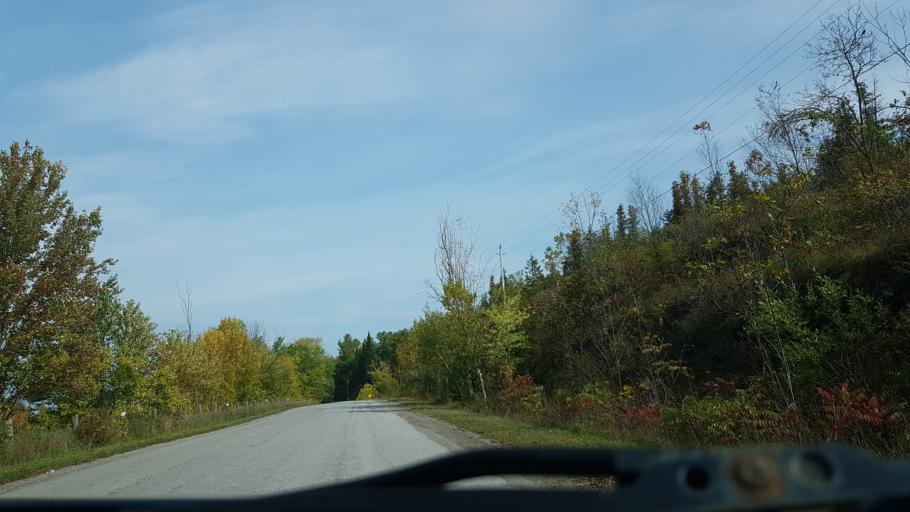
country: CA
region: Ontario
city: Orillia
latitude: 44.6463
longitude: -79.1060
